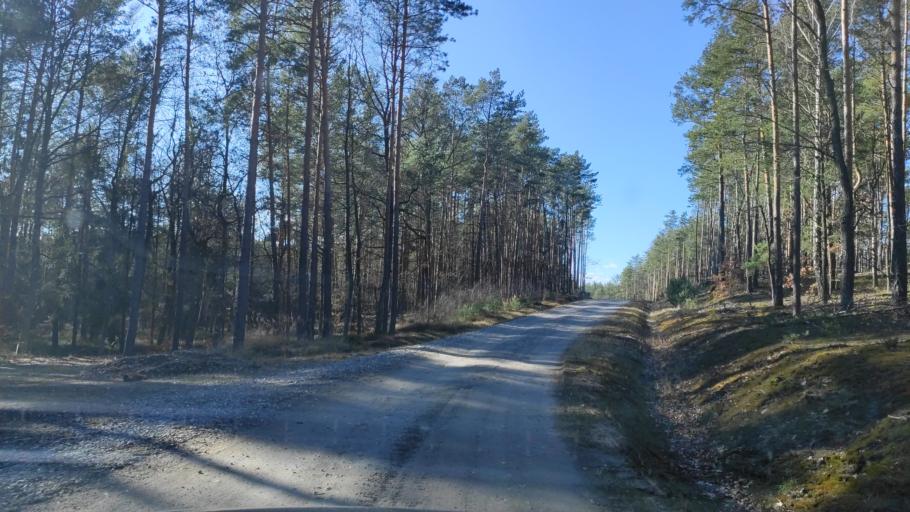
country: PL
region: Masovian Voivodeship
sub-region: Powiat radomski
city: Jedlnia-Letnisko
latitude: 51.4735
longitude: 21.2932
